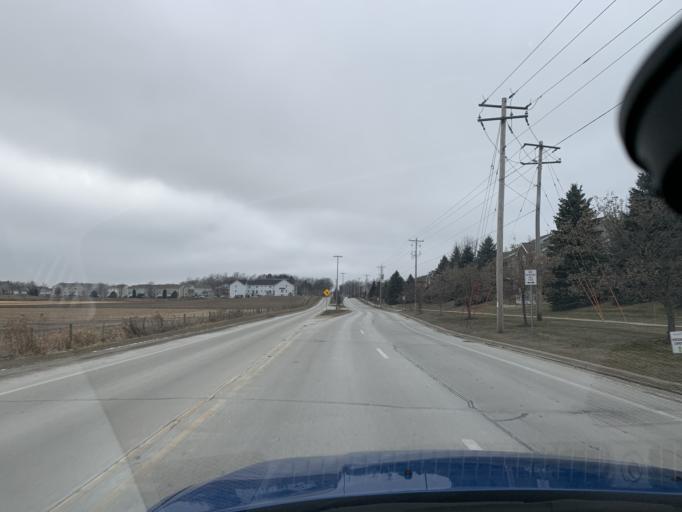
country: US
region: Wisconsin
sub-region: Dane County
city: Middleton
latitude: 43.0748
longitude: -89.5438
